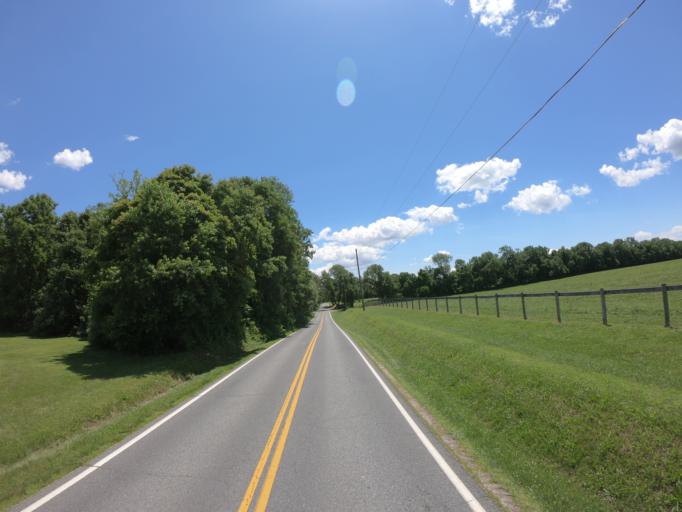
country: US
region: Delaware
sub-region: New Castle County
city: Middletown
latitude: 39.4710
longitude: -75.7791
